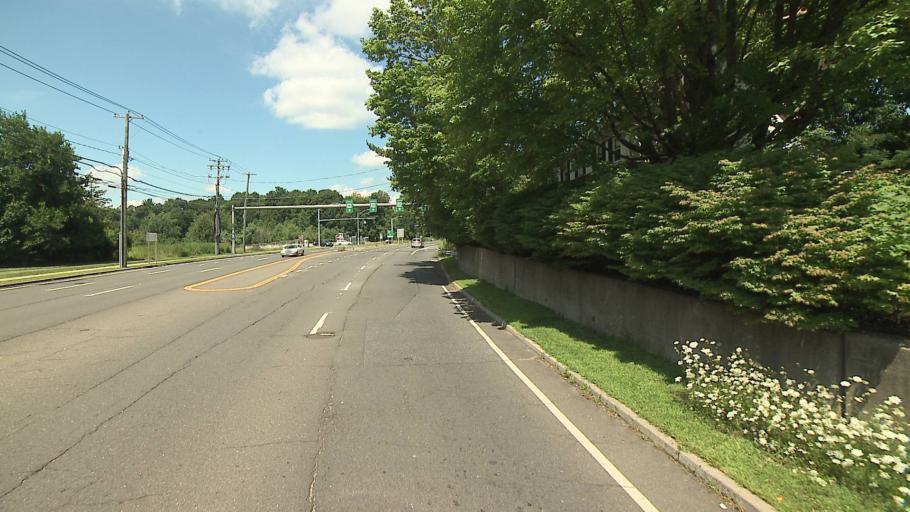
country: US
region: Connecticut
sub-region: Fairfield County
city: Trumbull
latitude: 41.2310
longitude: -73.2202
